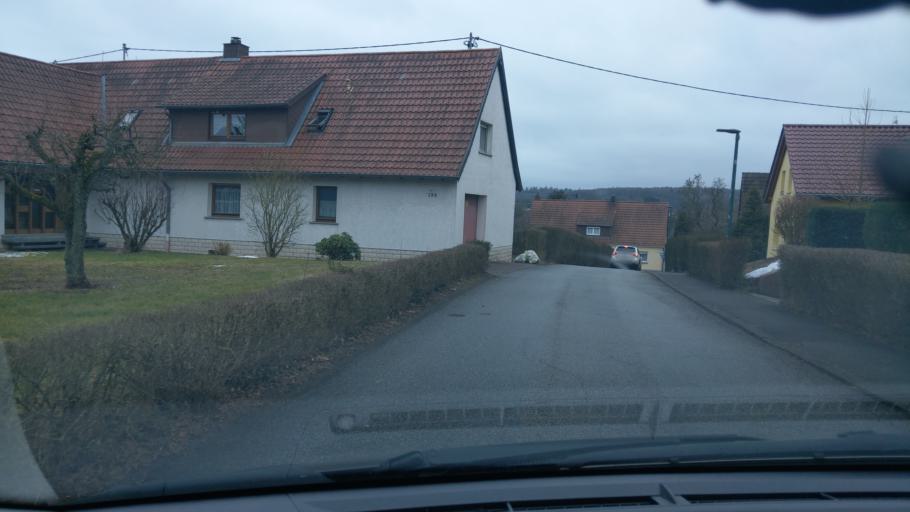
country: DE
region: Saarland
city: Ottweiler
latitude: 49.3752
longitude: 7.1679
